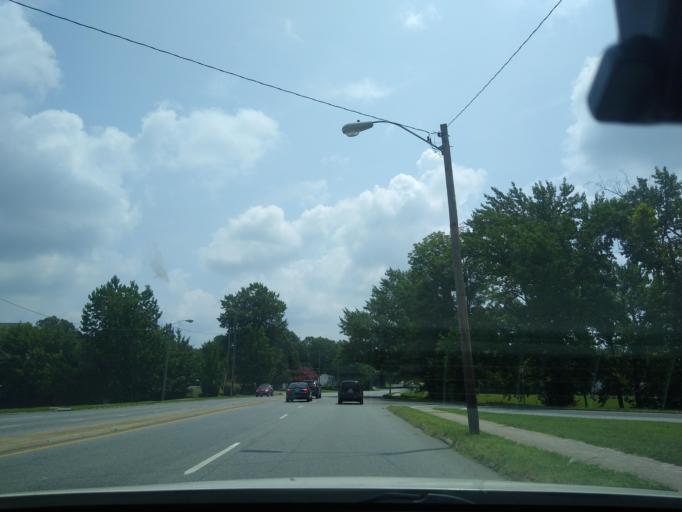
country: US
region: North Carolina
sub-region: Guilford County
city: Greensboro
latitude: 36.0643
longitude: -79.7705
